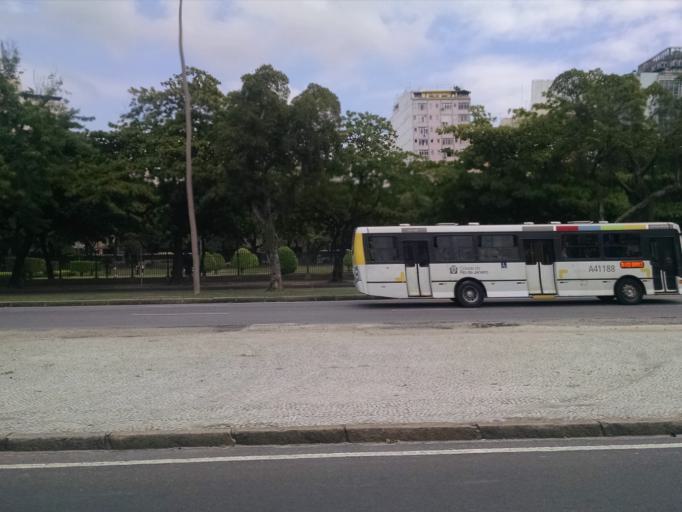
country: BR
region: Rio de Janeiro
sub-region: Rio De Janeiro
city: Rio de Janeiro
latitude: -22.9161
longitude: -43.1749
